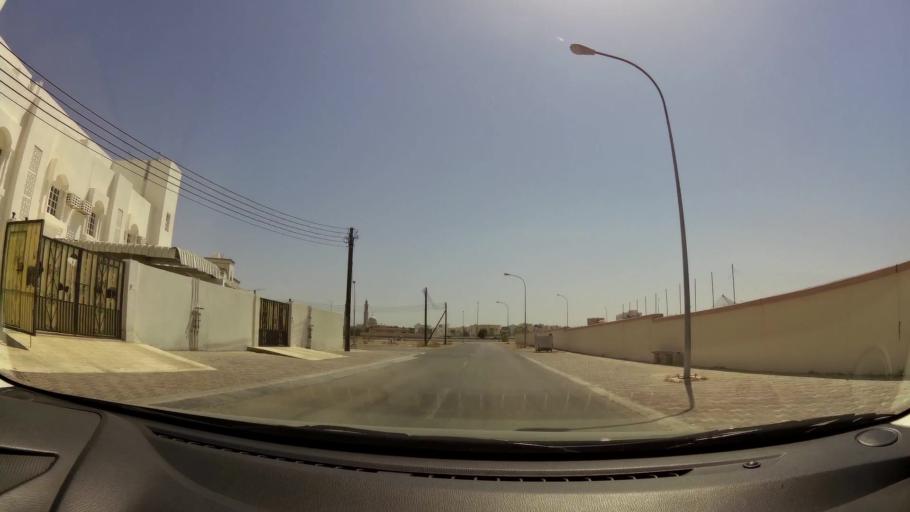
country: OM
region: Muhafazat Masqat
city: As Sib al Jadidah
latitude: 23.6170
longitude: 58.2159
